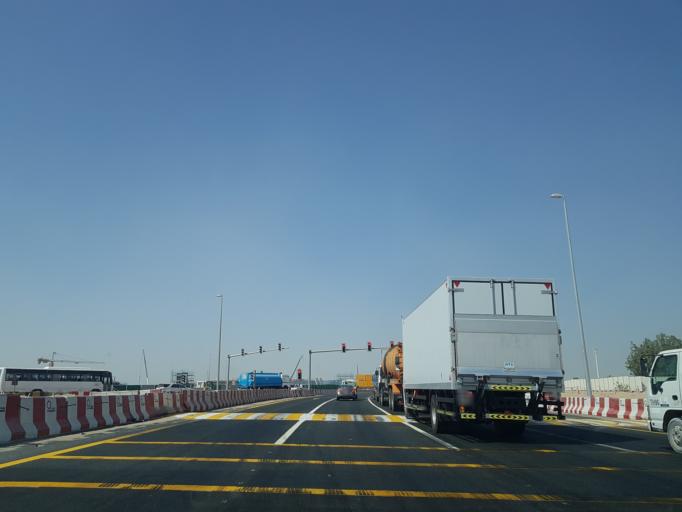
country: AE
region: Dubai
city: Dubai
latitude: 24.9641
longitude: 55.1864
